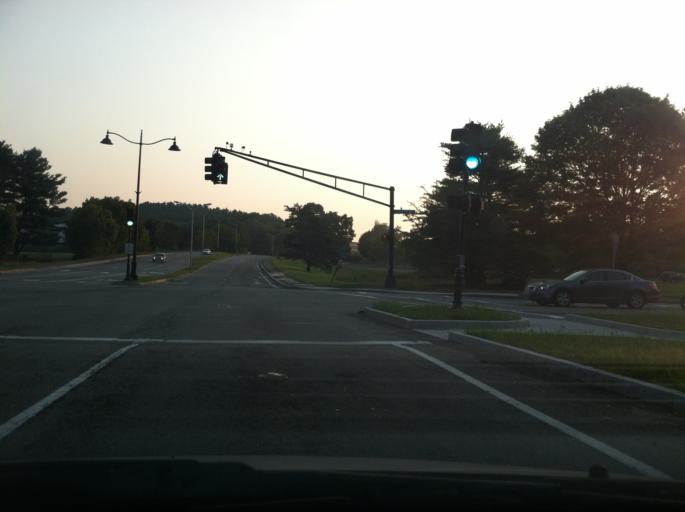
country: US
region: Massachusetts
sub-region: Middlesex County
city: Burlington
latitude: 42.4883
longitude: -71.2014
